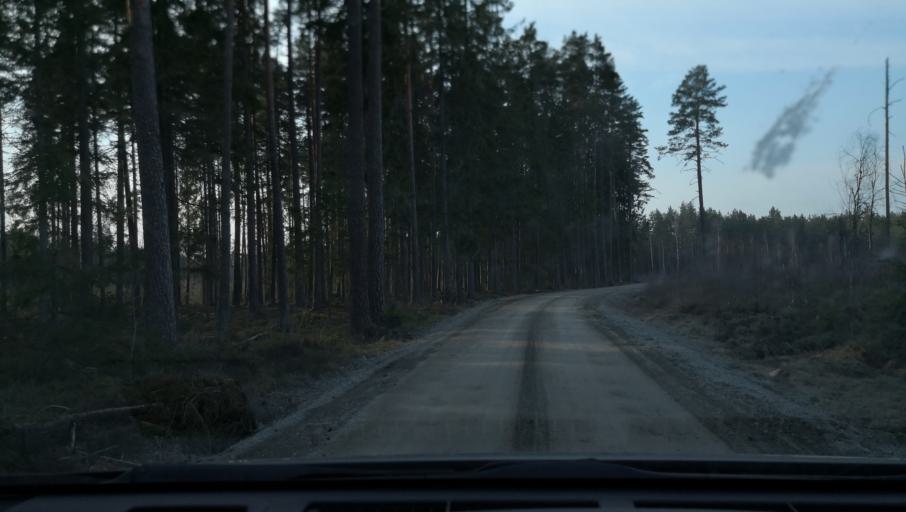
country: SE
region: OErebro
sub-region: Lindesbergs Kommun
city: Frovi
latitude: 59.3578
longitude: 15.3318
